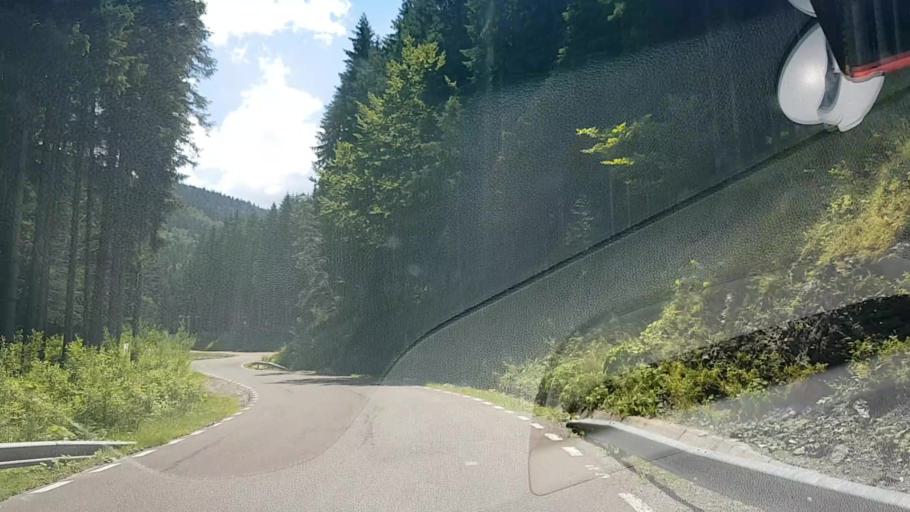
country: RO
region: Suceava
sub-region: Comuna Sadova
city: Sadova
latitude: 47.4731
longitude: 25.5040
